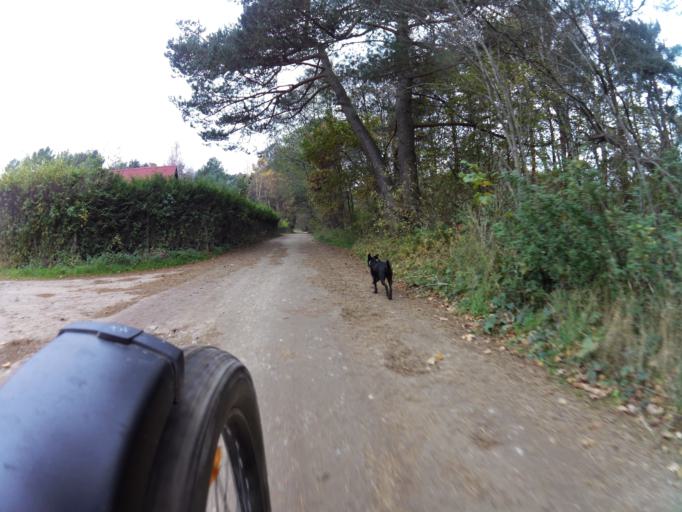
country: PL
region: Pomeranian Voivodeship
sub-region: Powiat pucki
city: Krokowa
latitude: 54.8285
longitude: 18.1049
